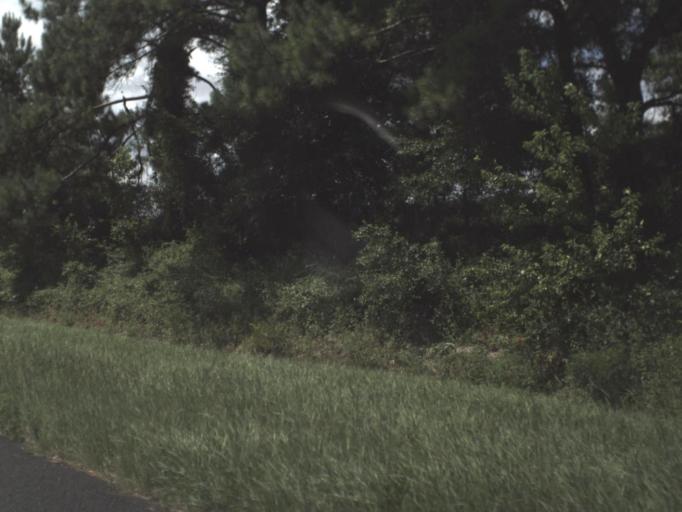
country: US
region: Florida
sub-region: Jefferson County
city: Monticello
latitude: 30.3682
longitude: -83.8051
